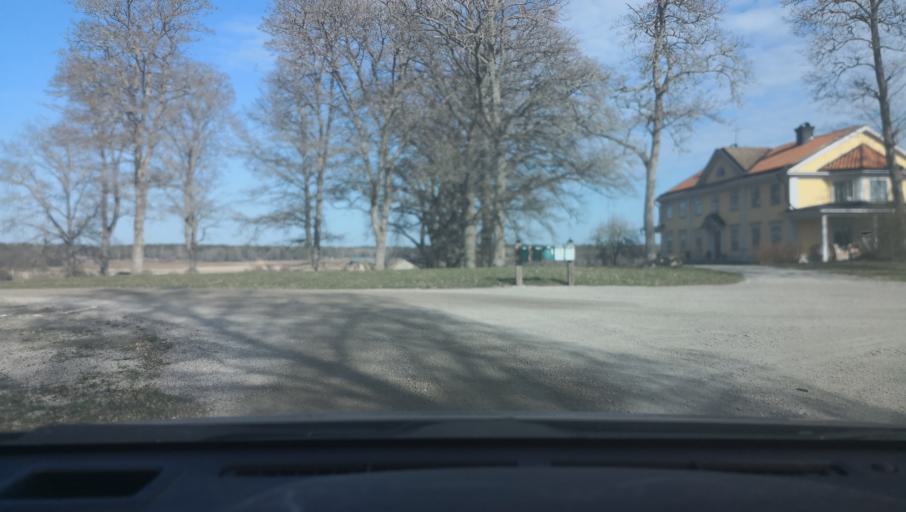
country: SE
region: Uppsala
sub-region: Heby Kommun
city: Morgongava
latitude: 59.8382
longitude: 16.9115
